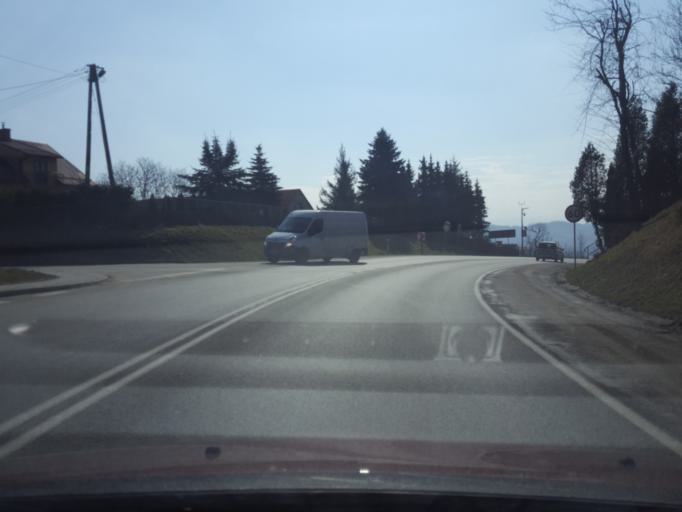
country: PL
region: Lesser Poland Voivodeship
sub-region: Powiat nowosadecki
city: Lososina Dolna
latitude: 49.7245
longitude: 20.6415
